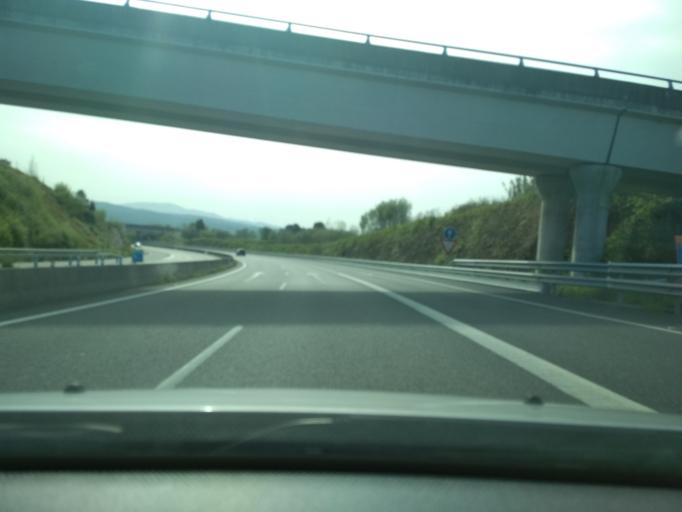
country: ES
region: Galicia
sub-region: Provincia da Coruna
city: Rianxo
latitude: 42.6696
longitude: -8.8271
